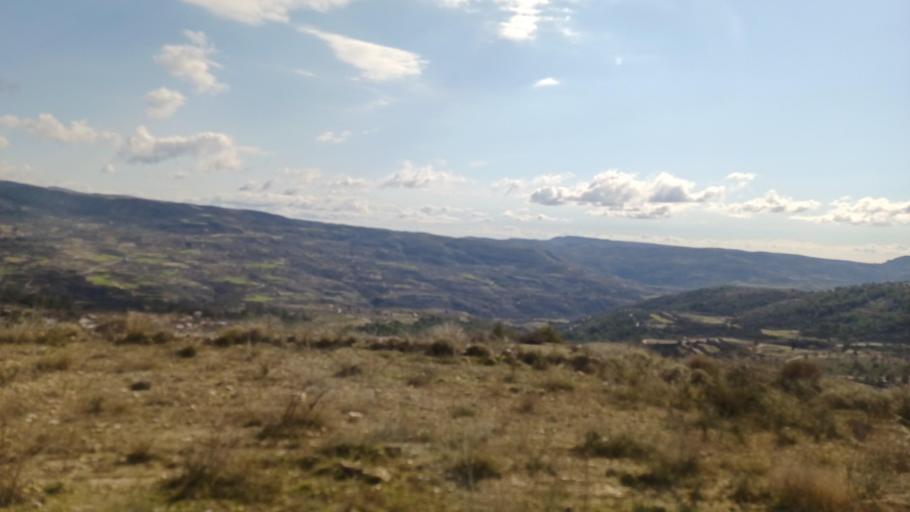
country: CY
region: Limassol
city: Pachna
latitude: 34.8497
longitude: 32.6935
